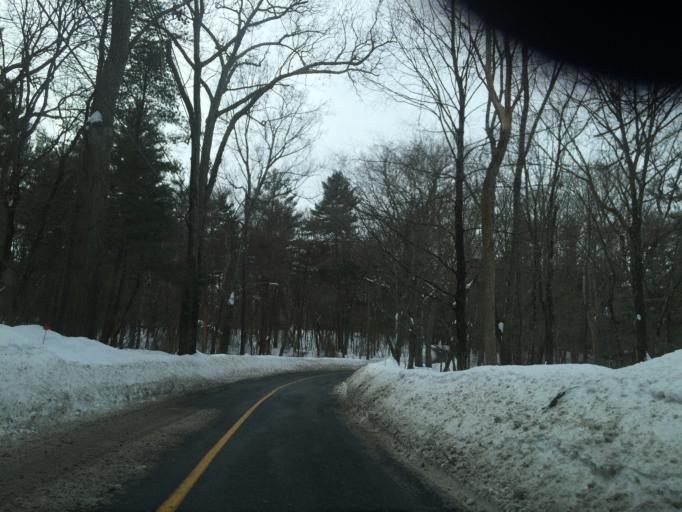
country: US
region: Massachusetts
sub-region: Middlesex County
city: Weston
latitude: 42.3827
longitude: -71.3091
